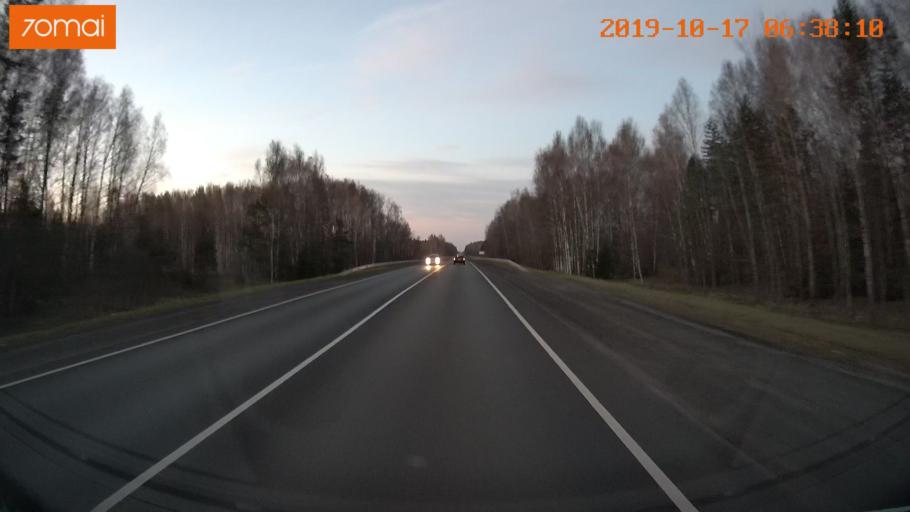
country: RU
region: Ivanovo
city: Novoye Leushino
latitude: 56.6594
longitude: 40.5897
